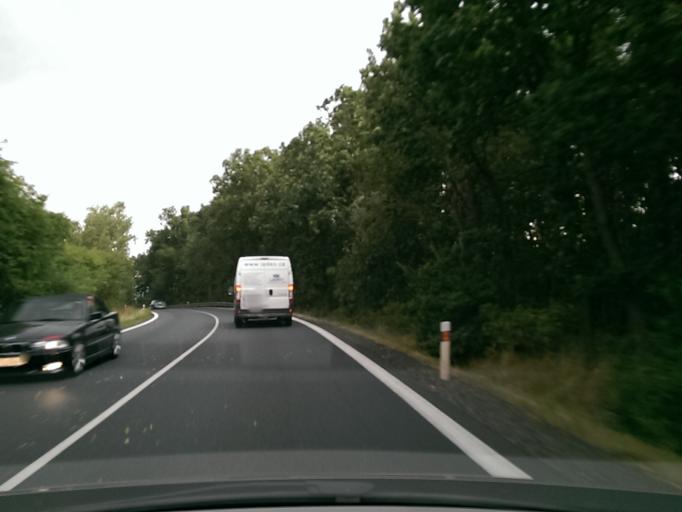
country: CZ
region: Central Bohemia
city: Loucen
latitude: 50.2646
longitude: 14.9750
